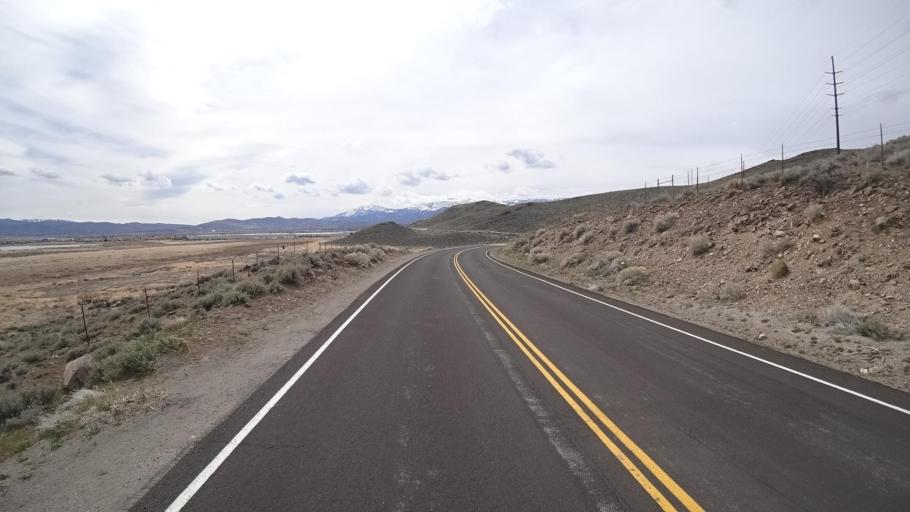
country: US
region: Nevada
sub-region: Washoe County
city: Sparks
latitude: 39.4643
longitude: -119.7367
